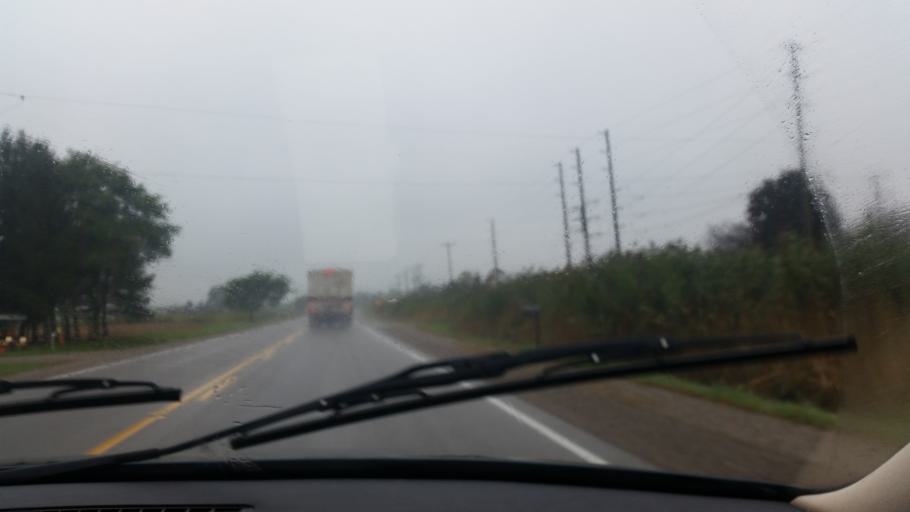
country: CA
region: Ontario
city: South Huron
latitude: 43.1642
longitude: -81.3645
